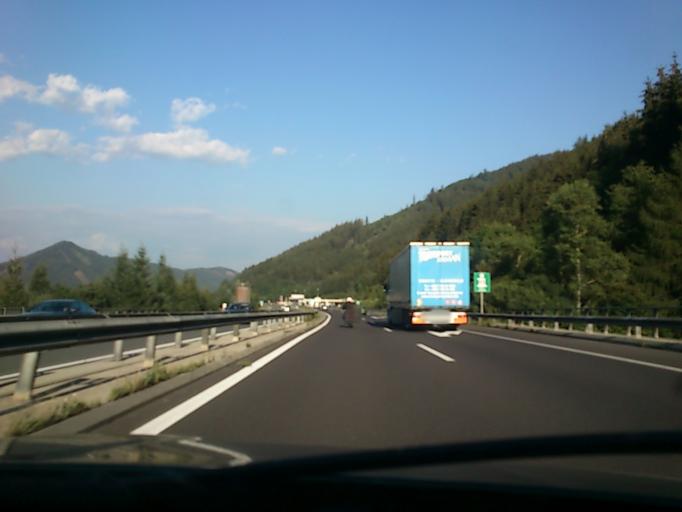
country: AT
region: Styria
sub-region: Politischer Bezirk Leoben
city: Kammern im Liesingtal
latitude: 47.3867
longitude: 14.8913
